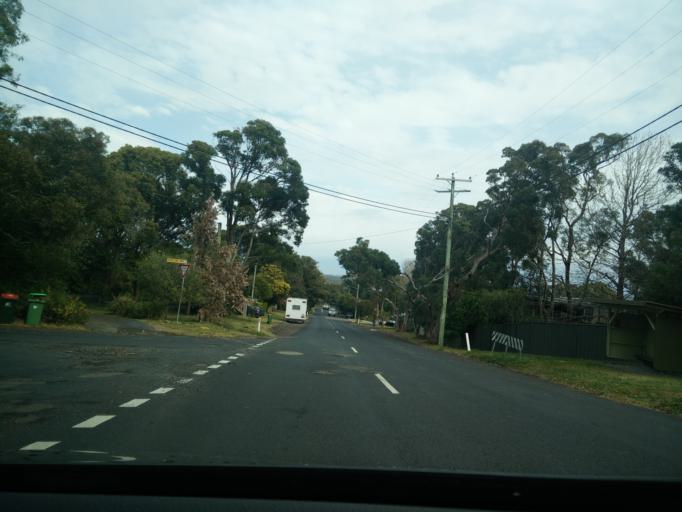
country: AU
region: New South Wales
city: Booker Bay
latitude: -33.5224
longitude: 151.3714
